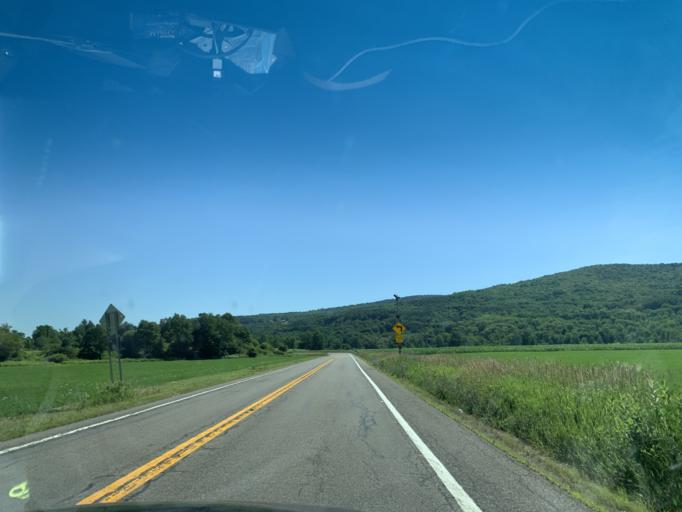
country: US
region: New York
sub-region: Chenango County
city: New Berlin
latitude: 42.5201
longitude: -75.3943
